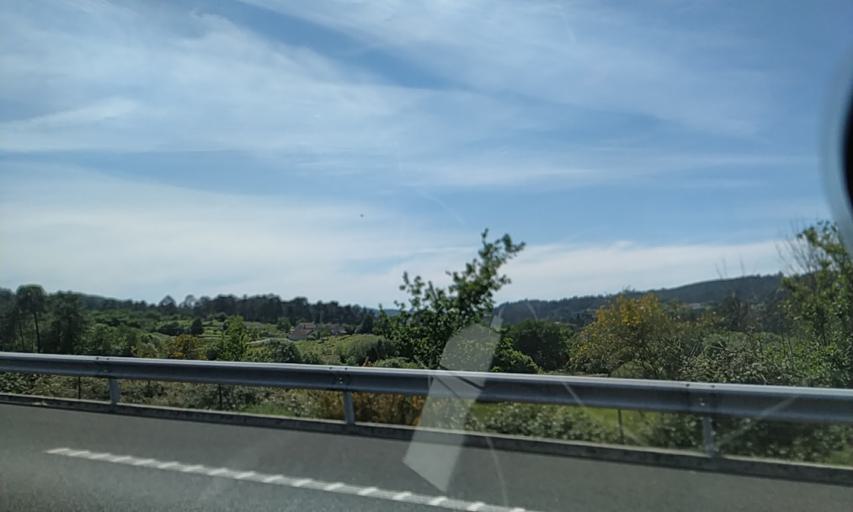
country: ES
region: Galicia
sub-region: Provincia de Pontevedra
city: Portas
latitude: 42.5501
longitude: -8.6675
